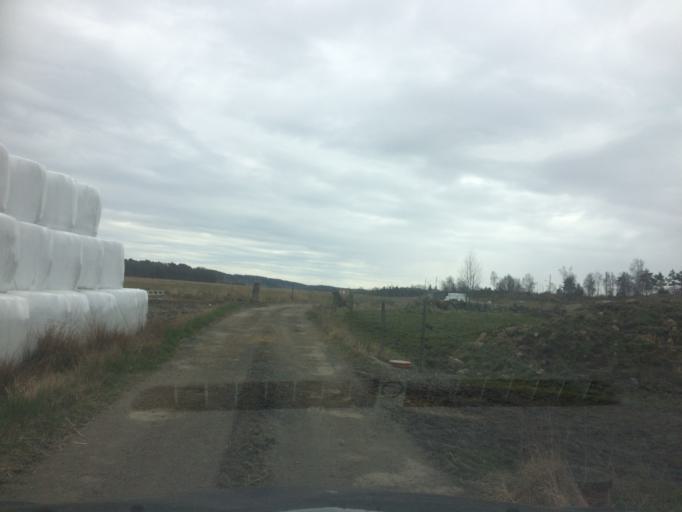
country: SE
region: Vaestra Goetaland
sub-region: Kungalvs Kommun
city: Kungalv
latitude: 57.8077
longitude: 11.8764
